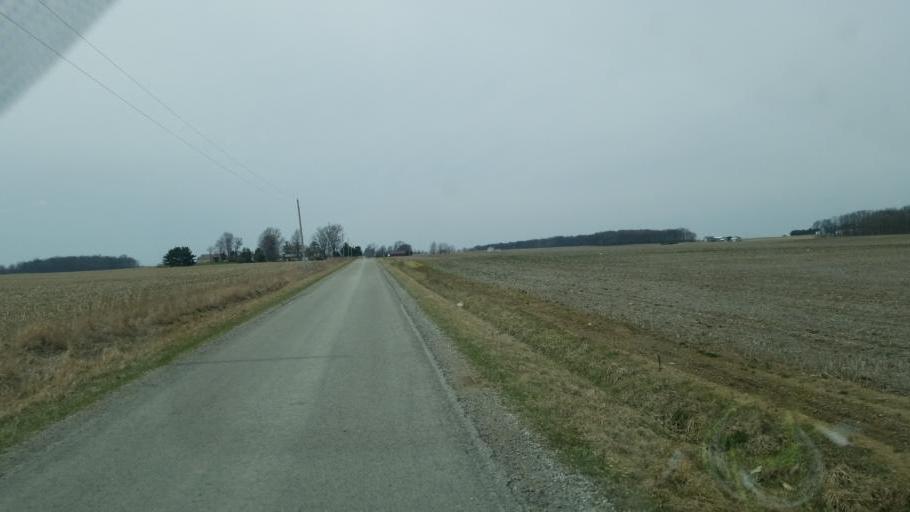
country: US
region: Ohio
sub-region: Huron County
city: Greenwich
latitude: 41.1445
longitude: -82.5027
